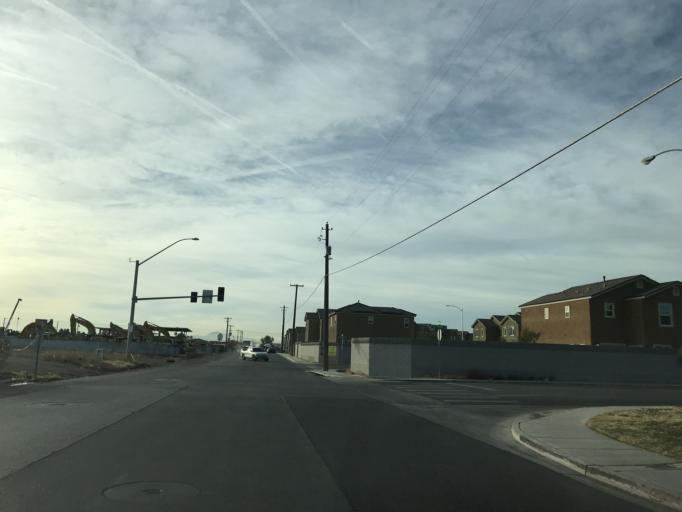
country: US
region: Nevada
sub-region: Clark County
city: Nellis Air Force Base
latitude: 36.2368
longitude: -115.0667
